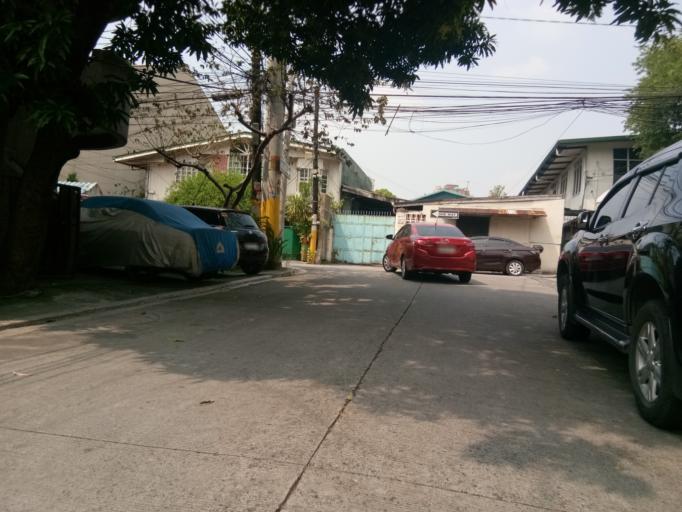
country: PH
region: Metro Manila
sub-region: San Juan
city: San Juan
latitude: 14.6138
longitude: 121.0528
